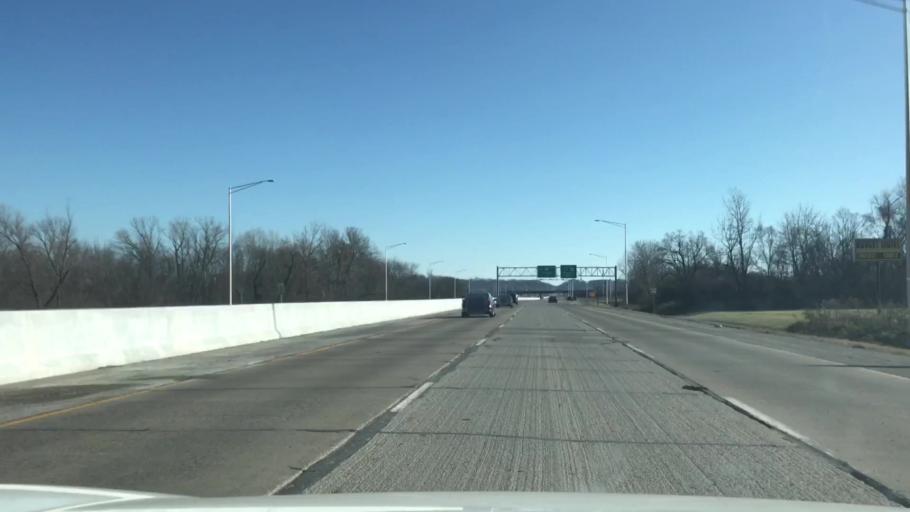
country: US
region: Illinois
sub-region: Saint Clair County
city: Alorton
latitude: 38.5882
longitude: -90.1143
